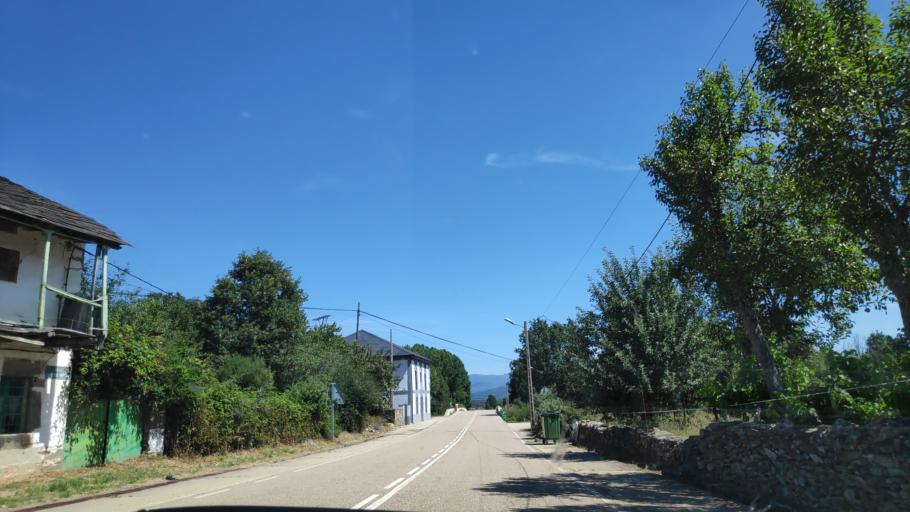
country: ES
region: Castille and Leon
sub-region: Provincia de Zamora
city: Puebla de Sanabria
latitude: 42.0401
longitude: -6.6662
